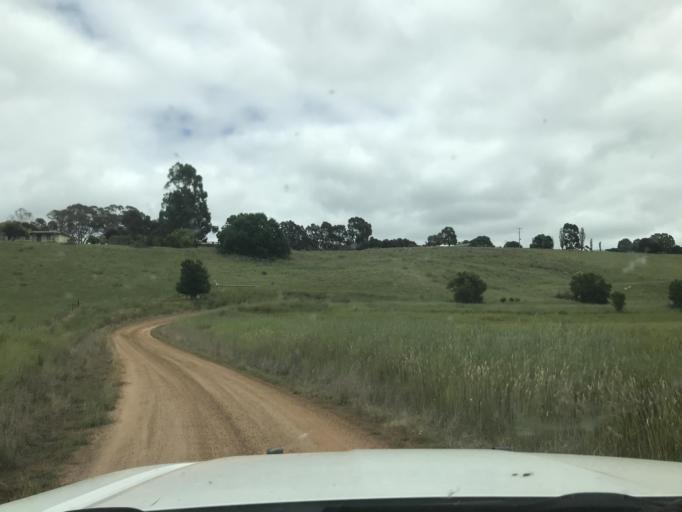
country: AU
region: South Australia
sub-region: Wattle Range
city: Penola
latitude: -37.3567
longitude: 141.2116
